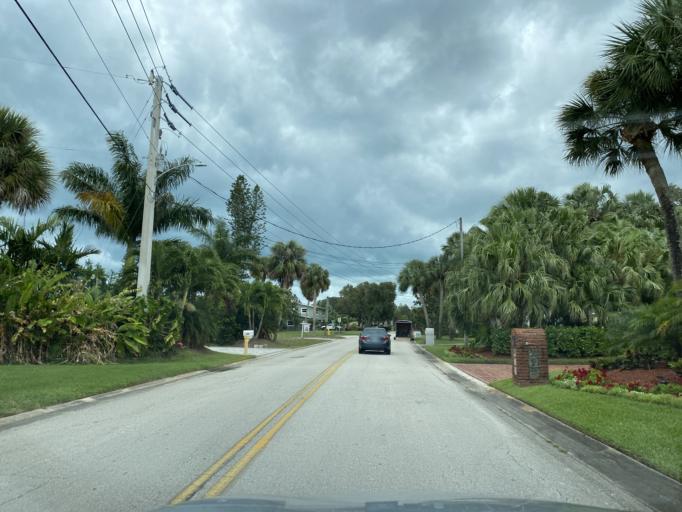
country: US
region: Florida
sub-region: Brevard County
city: Melbourne Beach
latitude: 28.0766
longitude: -80.5706
